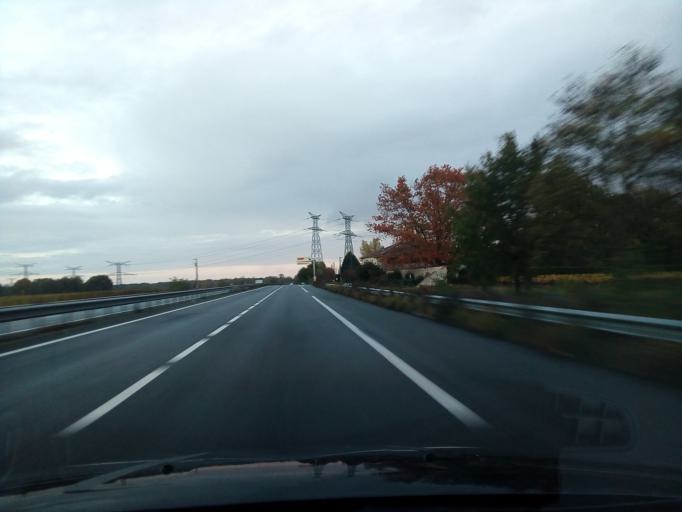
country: FR
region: Aquitaine
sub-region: Departement de la Gironde
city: Gauriaguet
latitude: 45.0486
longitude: -0.4089
